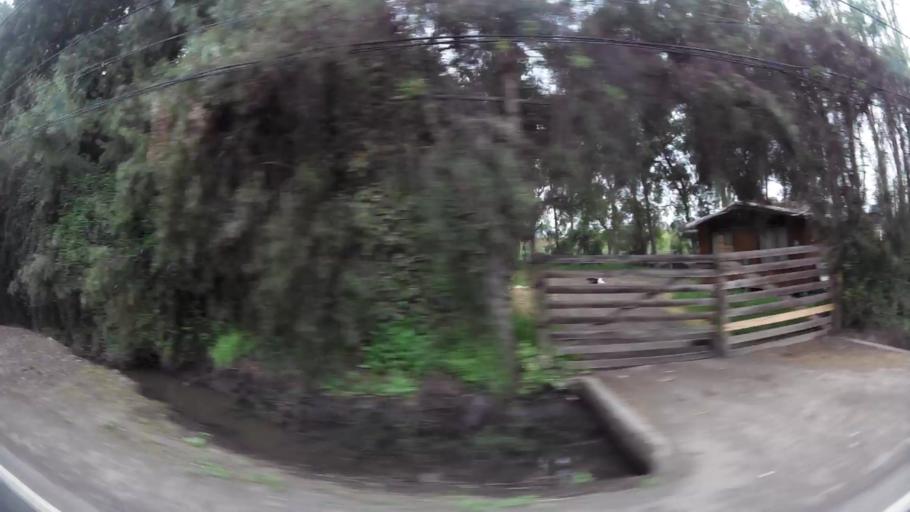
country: CL
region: Santiago Metropolitan
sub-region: Provincia de Chacabuco
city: Chicureo Abajo
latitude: -33.2566
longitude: -70.7627
